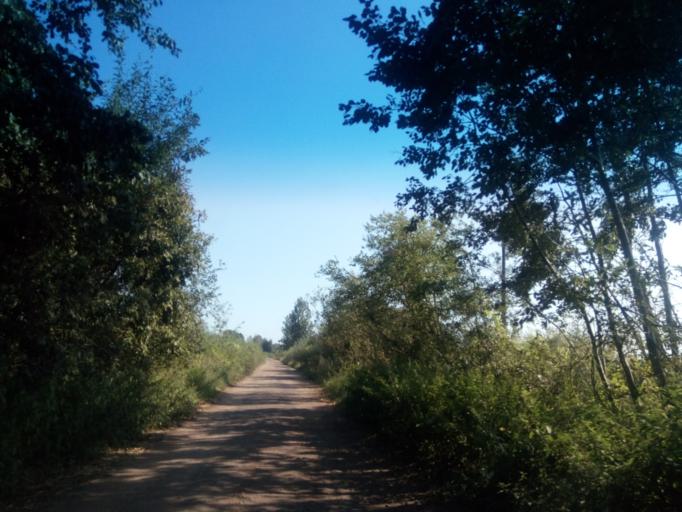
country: BY
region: Vitebsk
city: Dzisna
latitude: 55.6456
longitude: 28.2455
